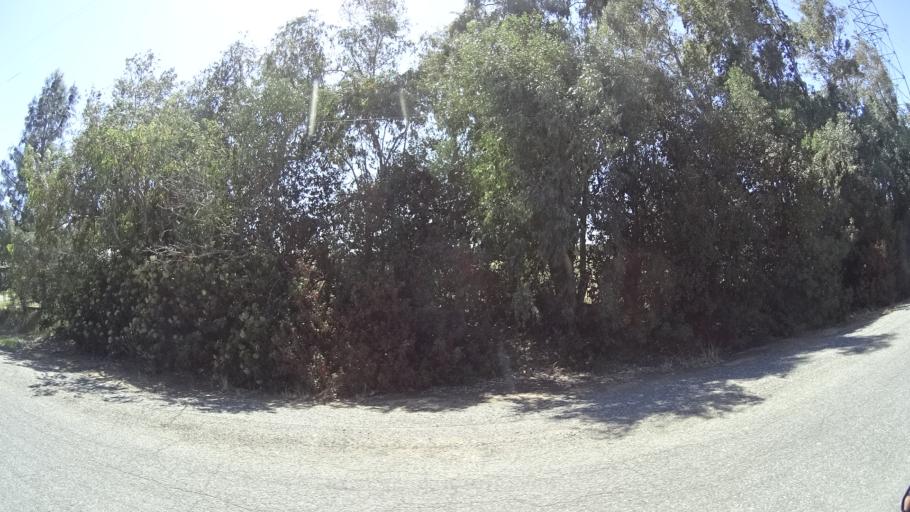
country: US
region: California
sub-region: Glenn County
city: Orland
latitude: 39.7977
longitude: -122.1703
